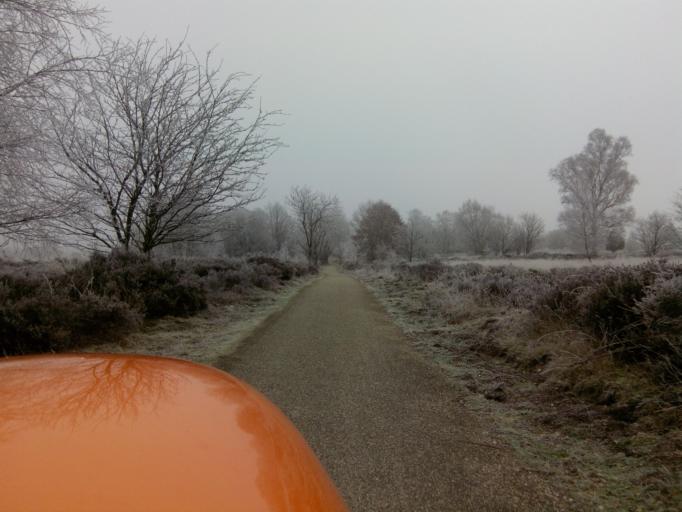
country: NL
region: Gelderland
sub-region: Gemeente Barneveld
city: Garderen
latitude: 52.2792
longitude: 5.6808
